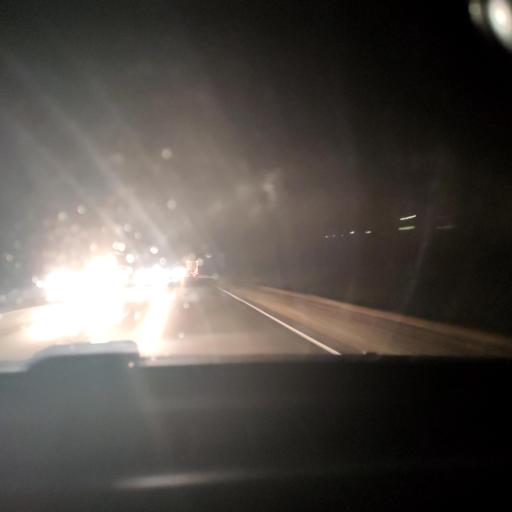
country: RU
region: Voronezj
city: Latnaya
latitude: 51.6321
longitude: 38.6654
